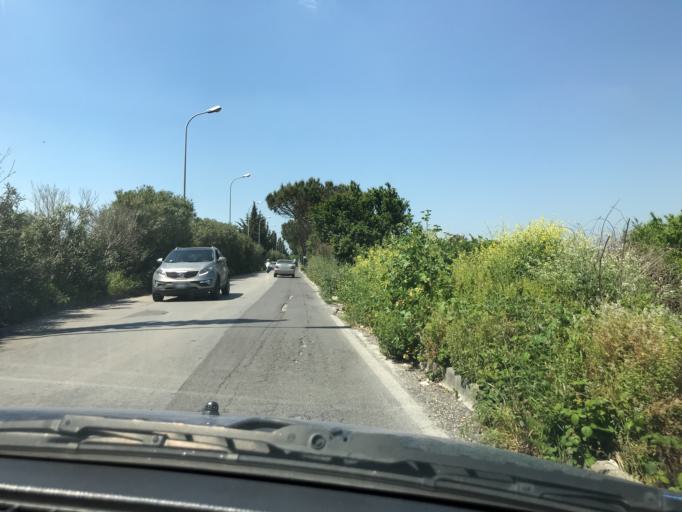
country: IT
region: Campania
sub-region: Provincia di Napoli
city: Calvizzano
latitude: 40.9097
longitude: 14.1942
